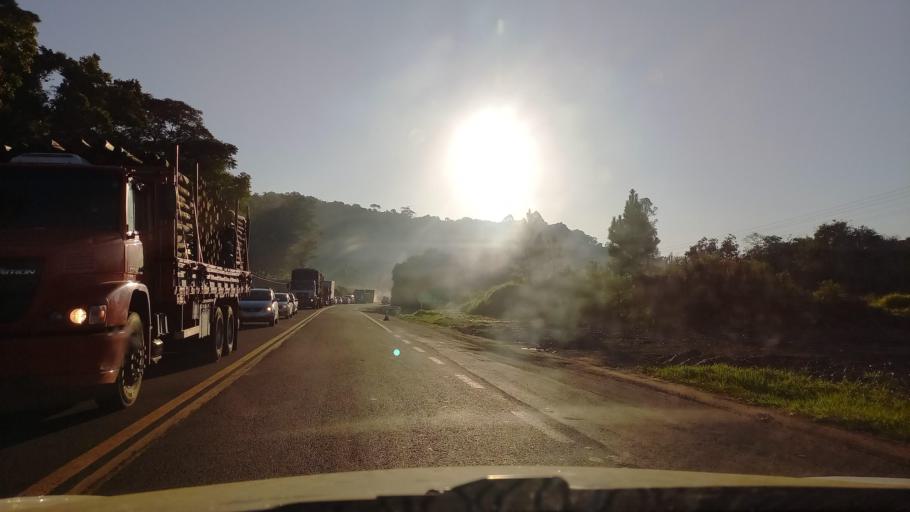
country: BR
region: Rio Grande do Sul
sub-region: Santa Cruz Do Sul
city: Santa Cruz do Sul
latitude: -29.6858
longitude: -52.4449
